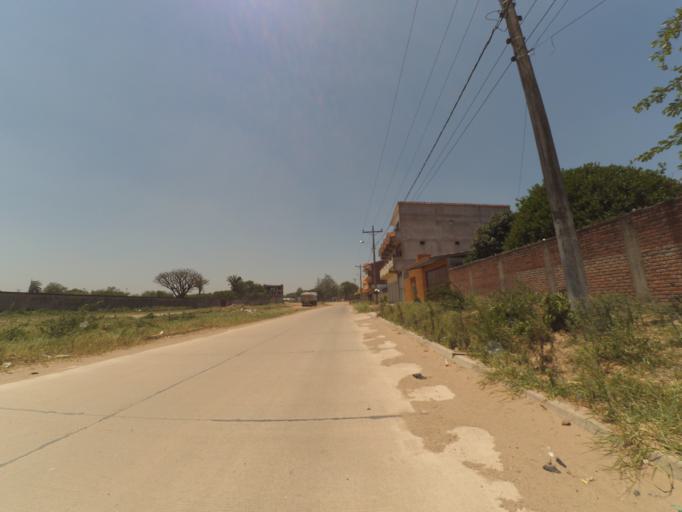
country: BO
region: Santa Cruz
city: Santa Cruz de la Sierra
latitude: -17.8530
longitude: -63.2397
